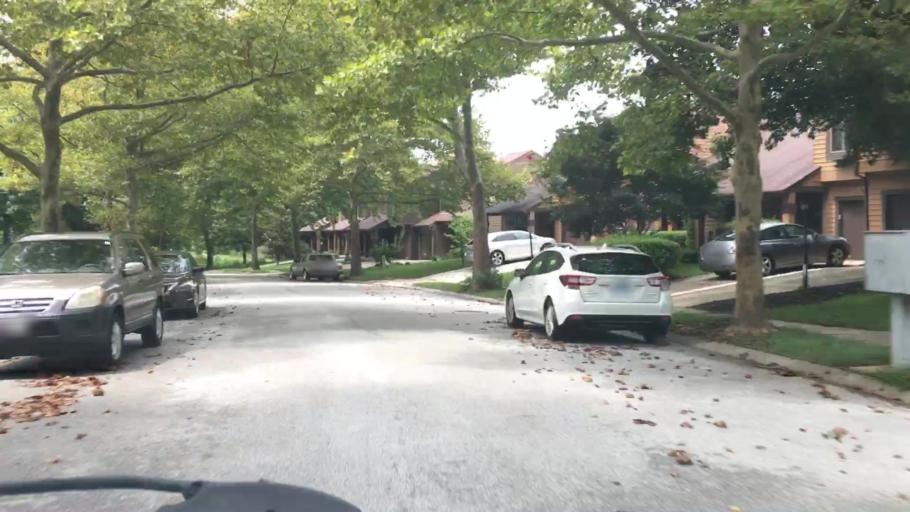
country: US
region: Maryland
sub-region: Howard County
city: Columbia
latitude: 39.1976
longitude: -76.8259
